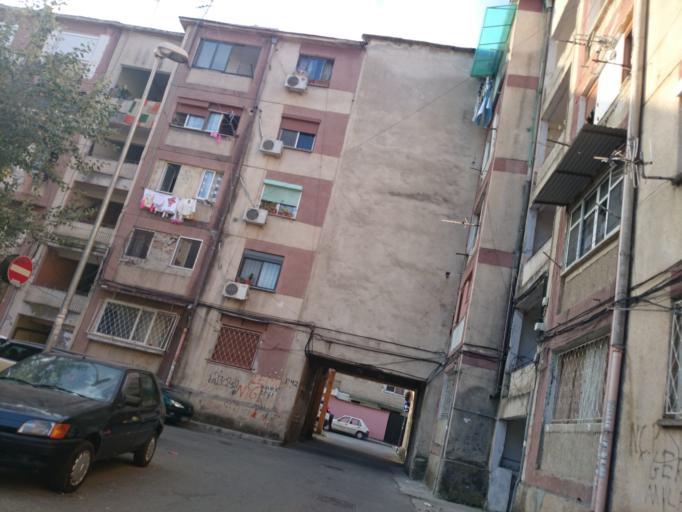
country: AL
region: Tirane
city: Tirana
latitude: 41.3250
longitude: 19.7948
